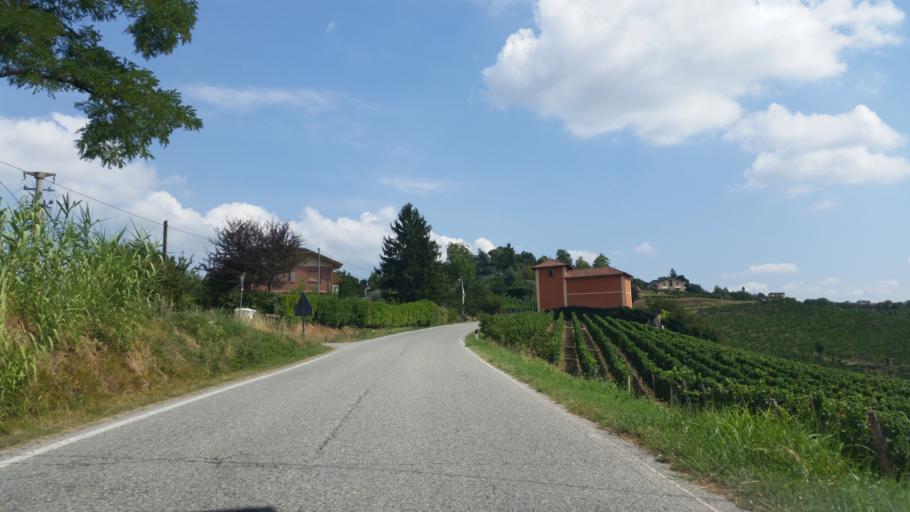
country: IT
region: Piedmont
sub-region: Provincia di Cuneo
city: Mango
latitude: 44.6912
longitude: 8.1436
